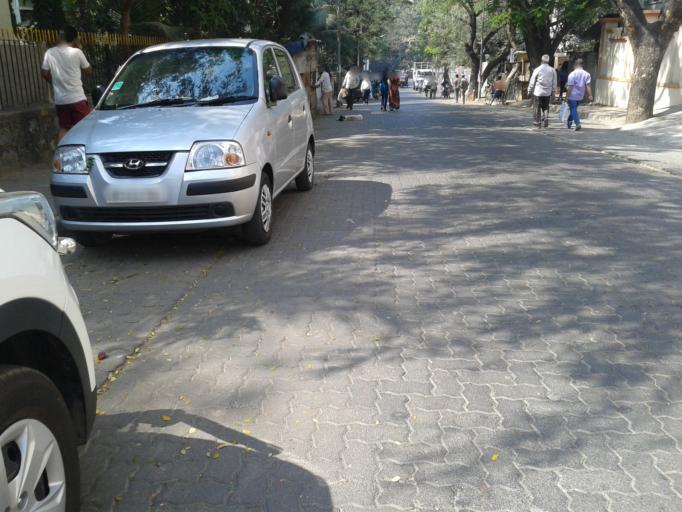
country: IN
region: Maharashtra
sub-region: Mumbai Suburban
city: Borivli
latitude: 19.2466
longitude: 72.8628
